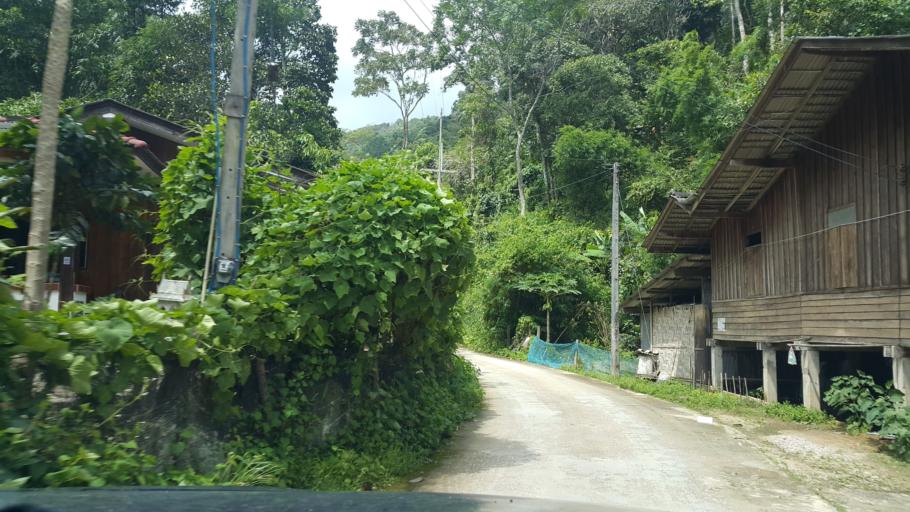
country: TH
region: Lampang
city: Wang Nuea
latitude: 19.0909
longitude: 99.3718
